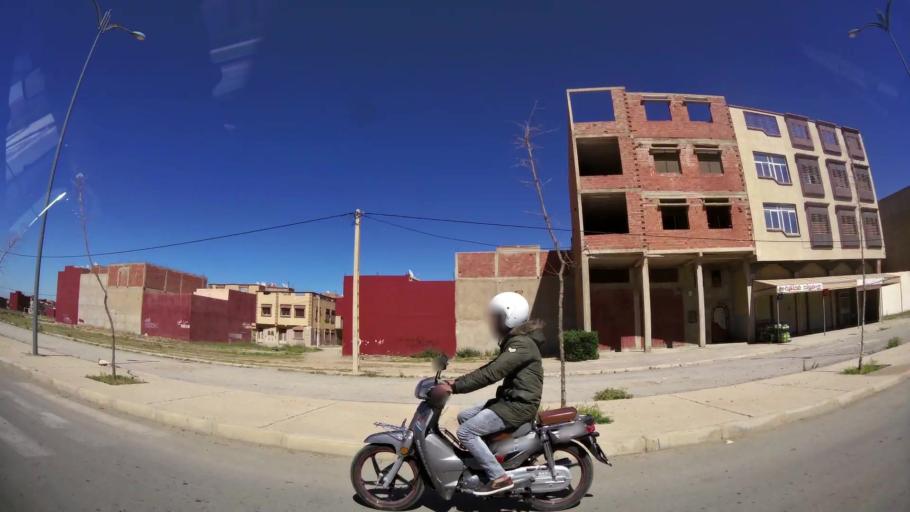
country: MA
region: Oriental
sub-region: Oujda-Angad
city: Oujda
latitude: 34.6772
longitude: -1.8596
